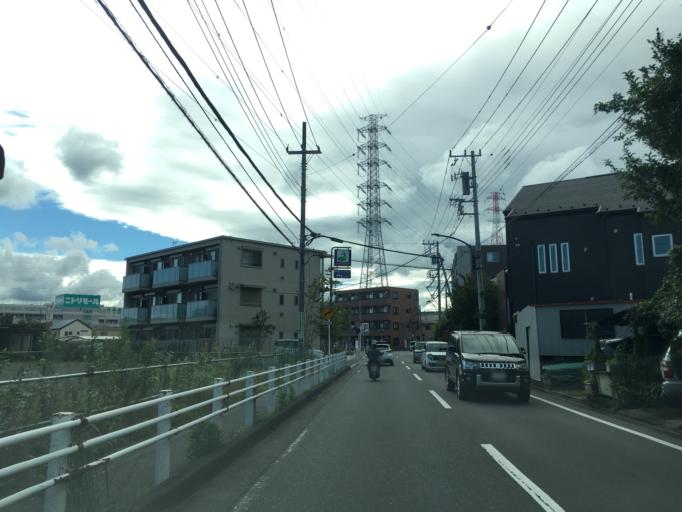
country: JP
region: Tokyo
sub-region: Machida-shi
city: Machida
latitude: 35.5570
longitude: 139.4137
